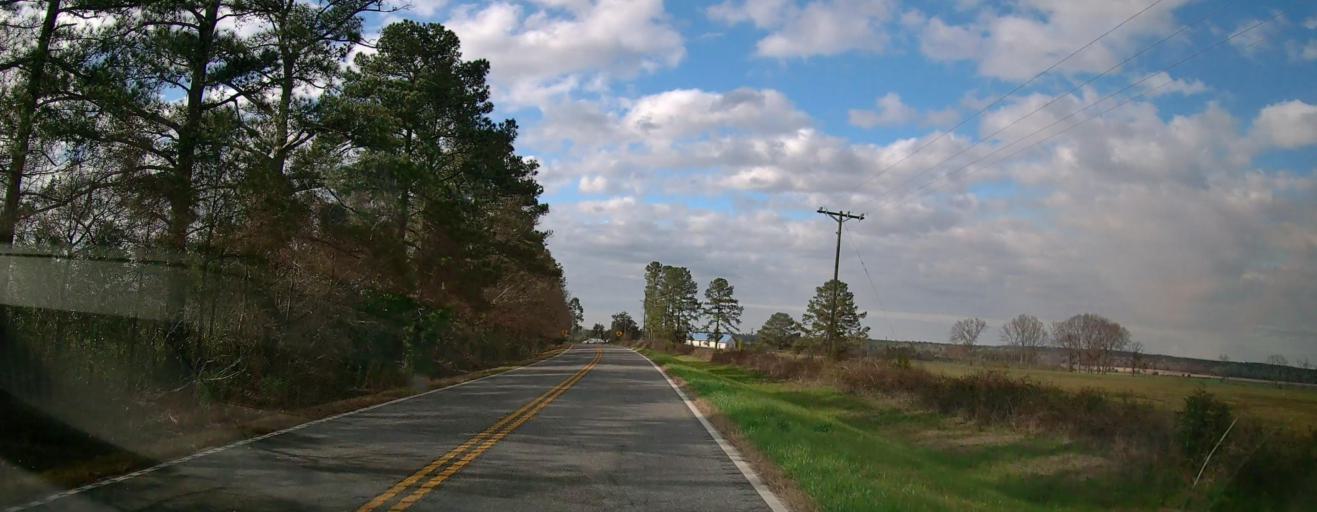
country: US
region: Georgia
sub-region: Marion County
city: Buena Vista
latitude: 32.4505
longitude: -84.4425
